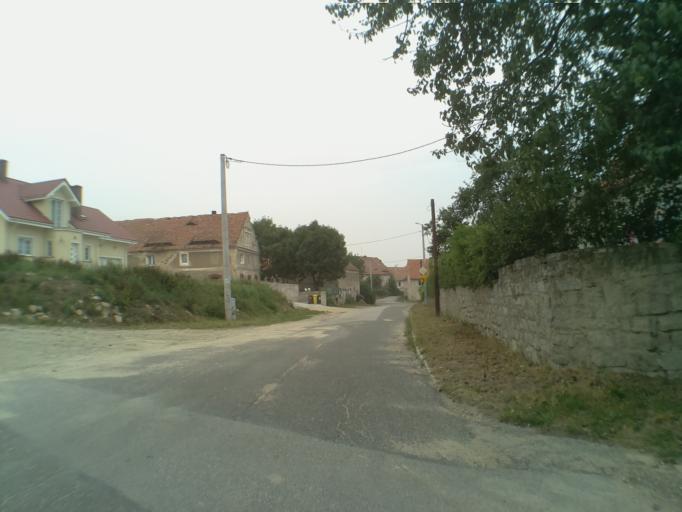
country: PL
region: Lower Silesian Voivodeship
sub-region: Powiat swidnicki
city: Strzegom
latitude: 50.9762
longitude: 16.3060
